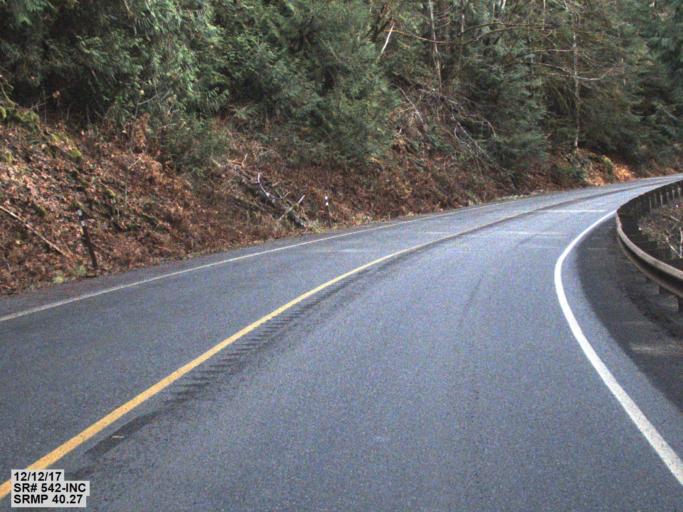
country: CA
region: British Columbia
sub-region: Fraser Valley Regional District
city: Chilliwack
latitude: 48.9105
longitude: -121.8162
